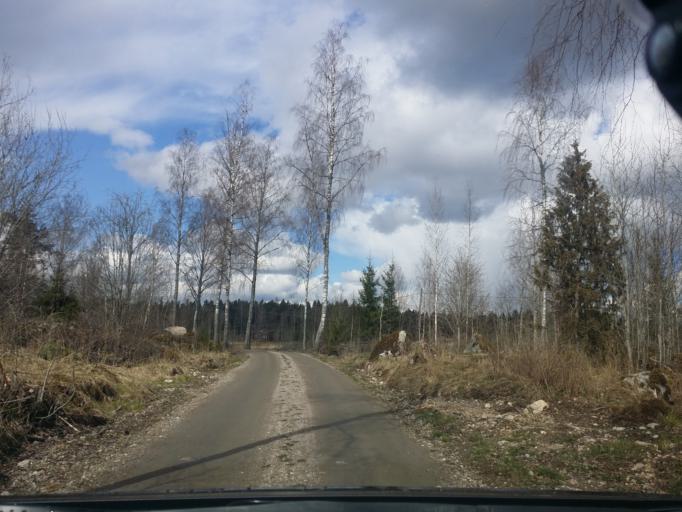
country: SE
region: Vaestmanland
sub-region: Sala Kommun
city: Sala
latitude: 59.9184
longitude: 16.6485
